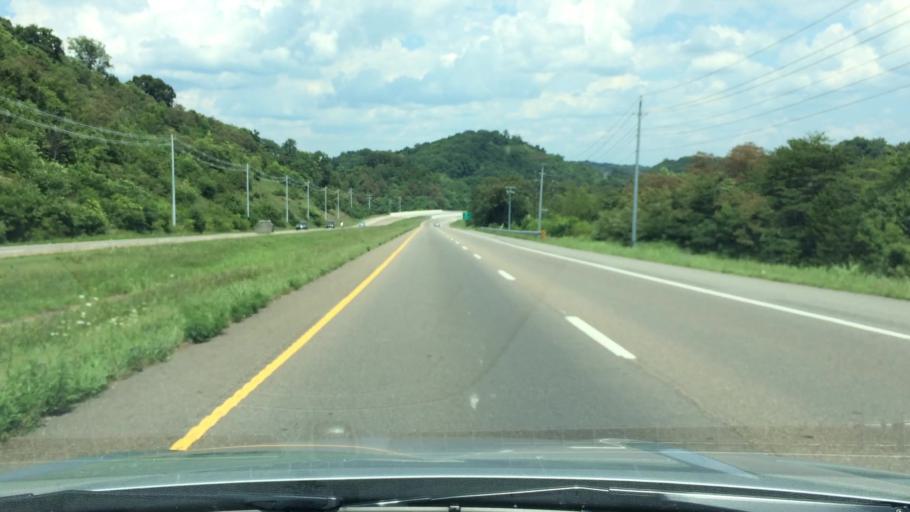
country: US
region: Tennessee
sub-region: Hamblen County
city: Morristown
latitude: 36.1900
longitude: -83.2843
